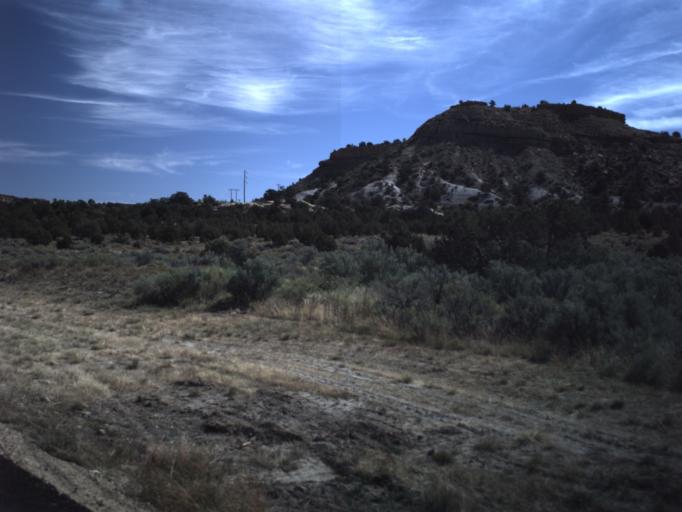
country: US
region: Utah
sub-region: Wayne County
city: Loa
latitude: 37.7729
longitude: -111.6486
